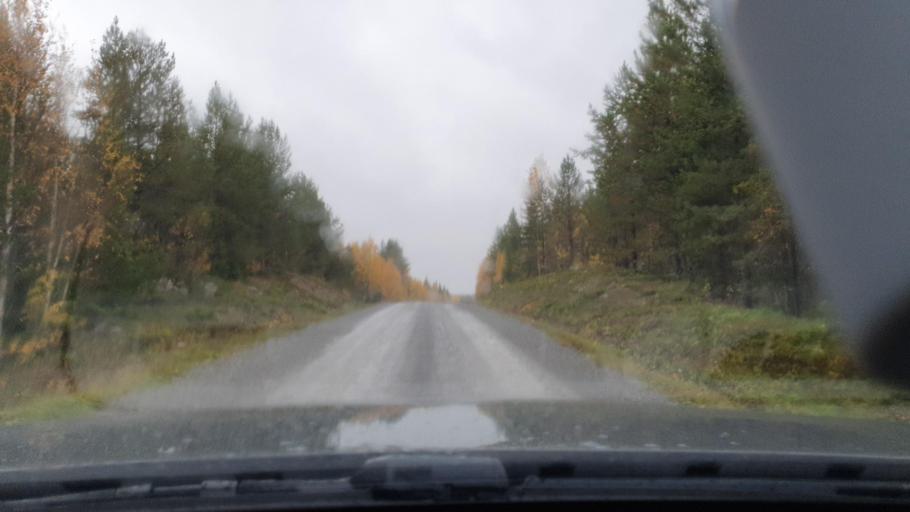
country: SE
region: Jaemtland
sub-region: Stroemsunds Kommun
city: Stroemsund
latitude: 63.5405
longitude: 15.5850
